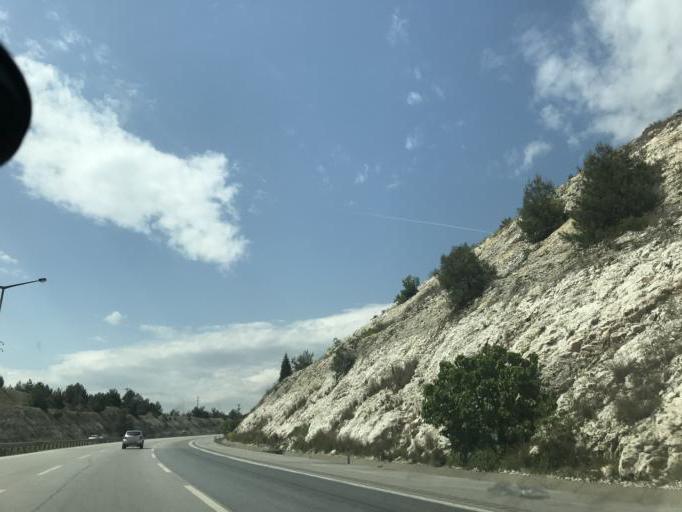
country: TR
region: Mersin
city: Tarsus
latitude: 37.1373
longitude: 34.8460
